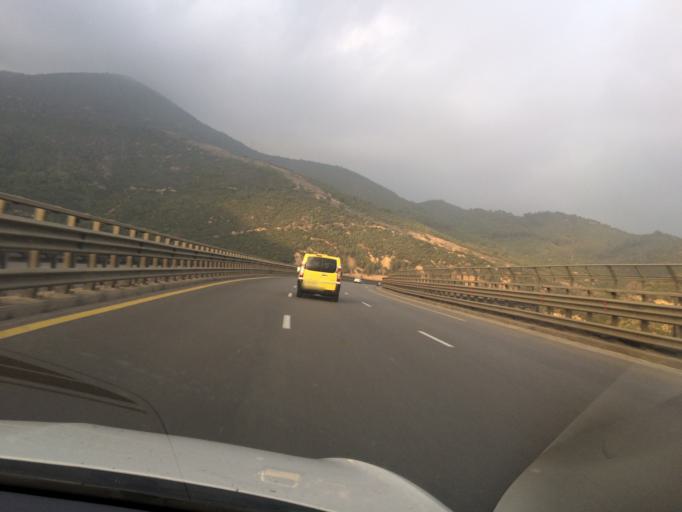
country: DZ
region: Tipaza
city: El Affroun
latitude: 36.3996
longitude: 2.5384
